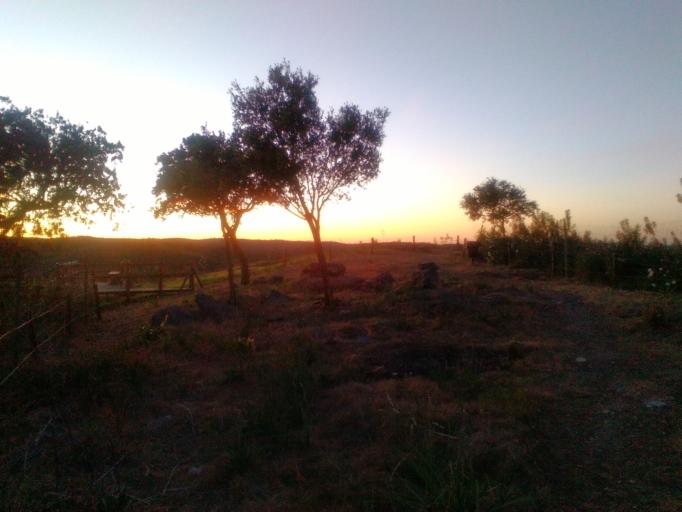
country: PT
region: Evora
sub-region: Reguengos de Monsaraz
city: Reguengos de Monsaraz
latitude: 38.3041
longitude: -7.5516
